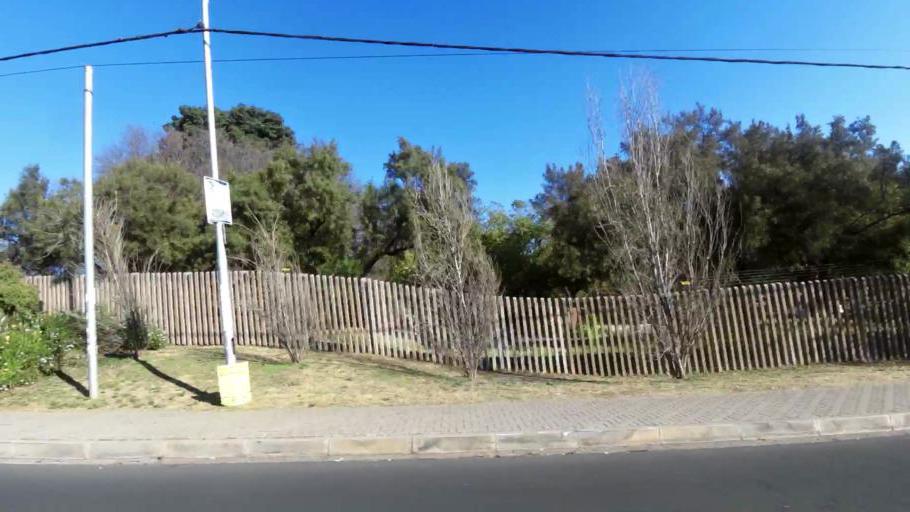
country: ZA
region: Gauteng
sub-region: City of Johannesburg Metropolitan Municipality
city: Johannesburg
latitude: -26.1890
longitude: 27.9971
